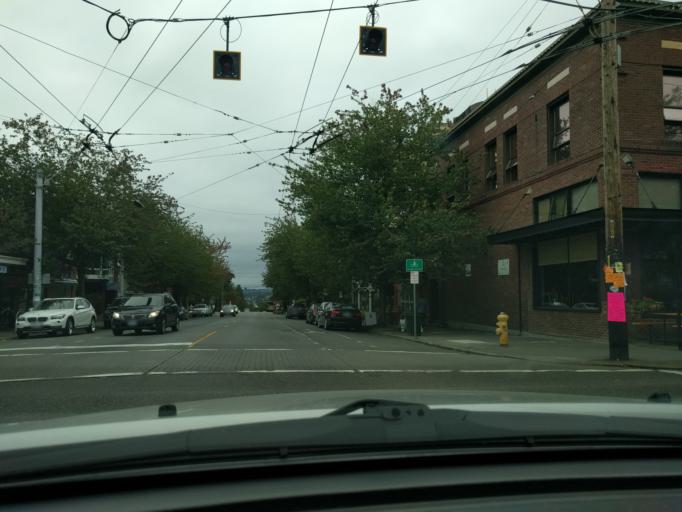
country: US
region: Washington
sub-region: King County
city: Seattle
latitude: 47.6385
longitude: -122.3569
